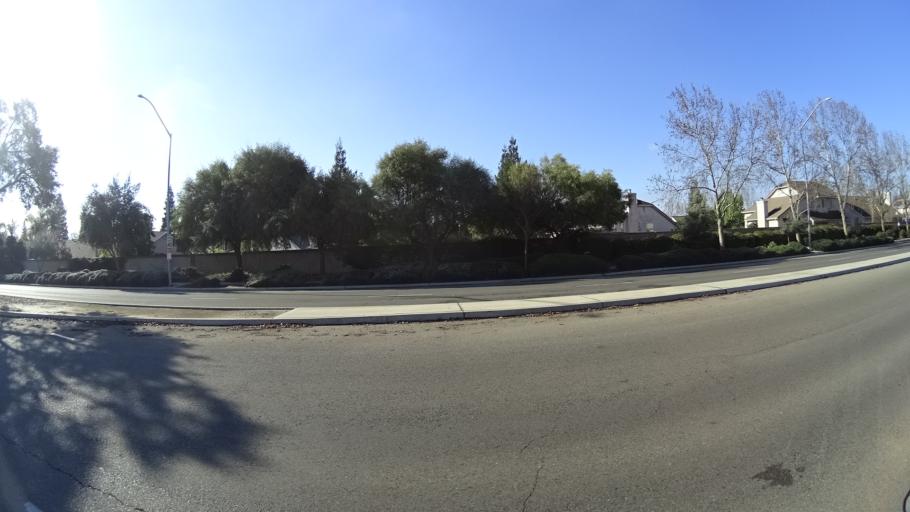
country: US
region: California
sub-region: Fresno County
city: West Park
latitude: 36.8219
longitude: -119.8827
